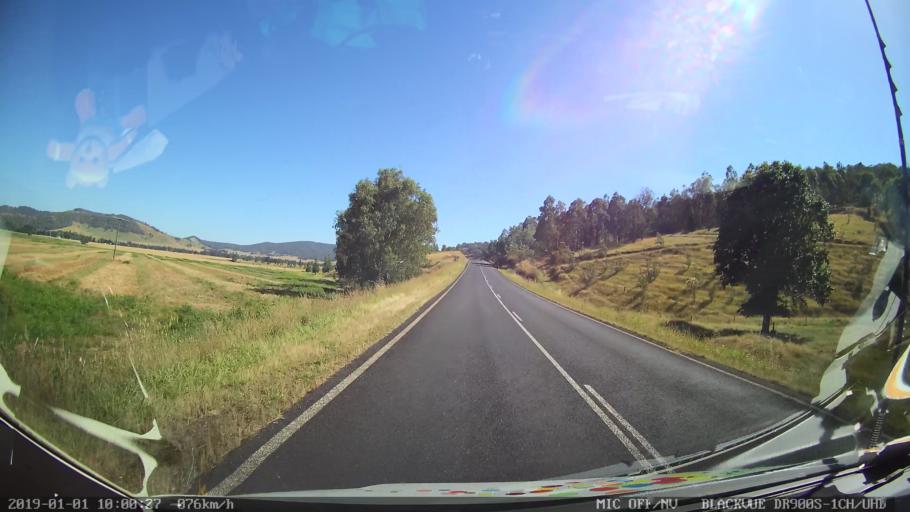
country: AU
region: New South Wales
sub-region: Snowy River
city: Jindabyne
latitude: -36.2021
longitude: 148.1018
